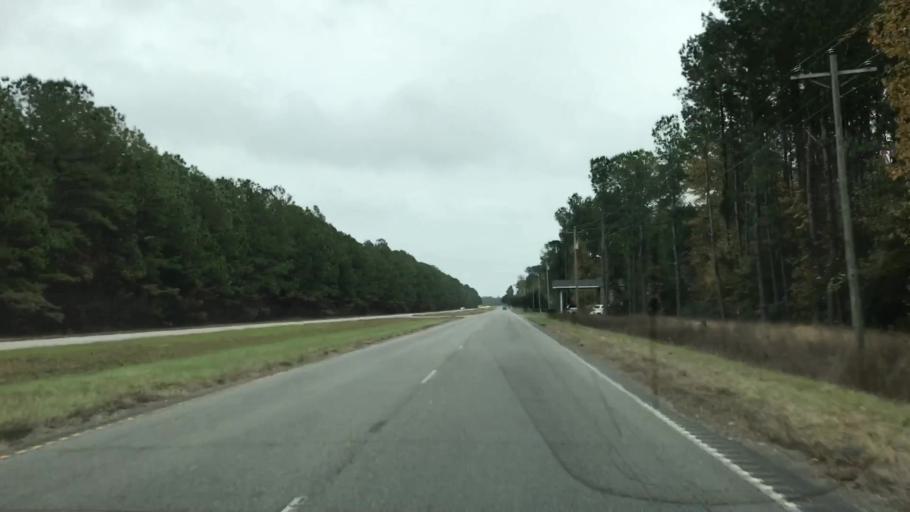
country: US
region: South Carolina
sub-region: Charleston County
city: Awendaw
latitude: 33.0378
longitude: -79.6114
